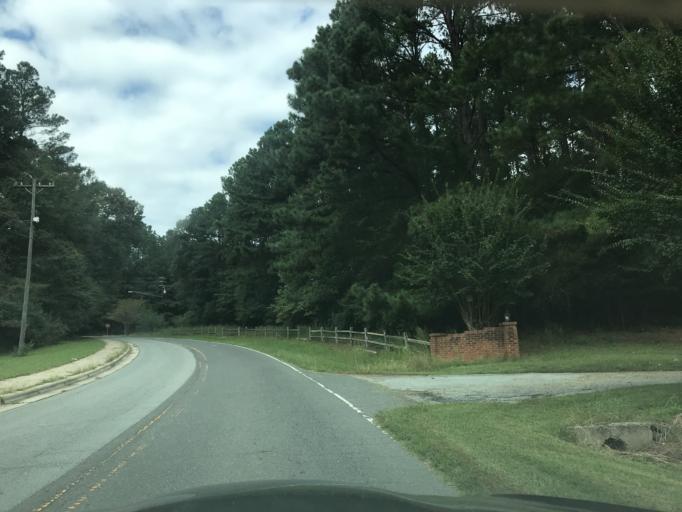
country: US
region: North Carolina
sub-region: Orange County
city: Carrboro
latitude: 35.9240
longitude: -79.0677
